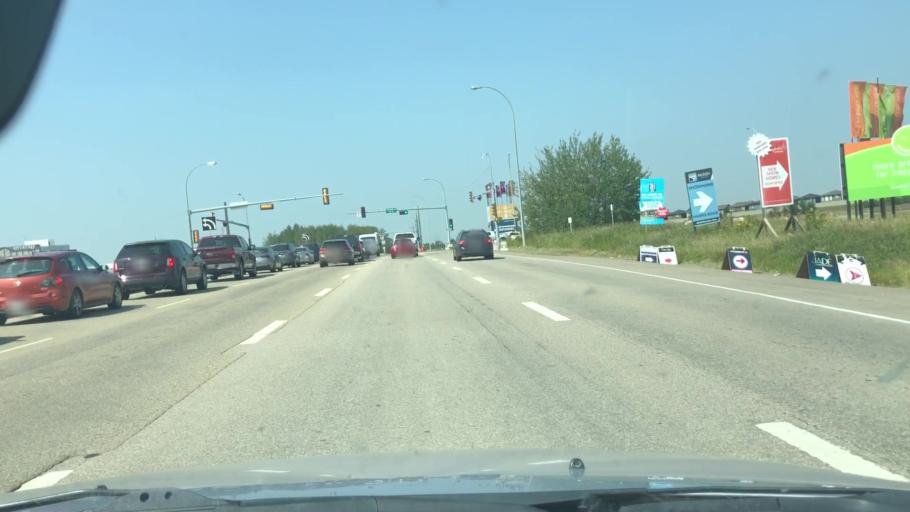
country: CA
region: Alberta
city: St. Albert
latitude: 53.5123
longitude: -113.6872
